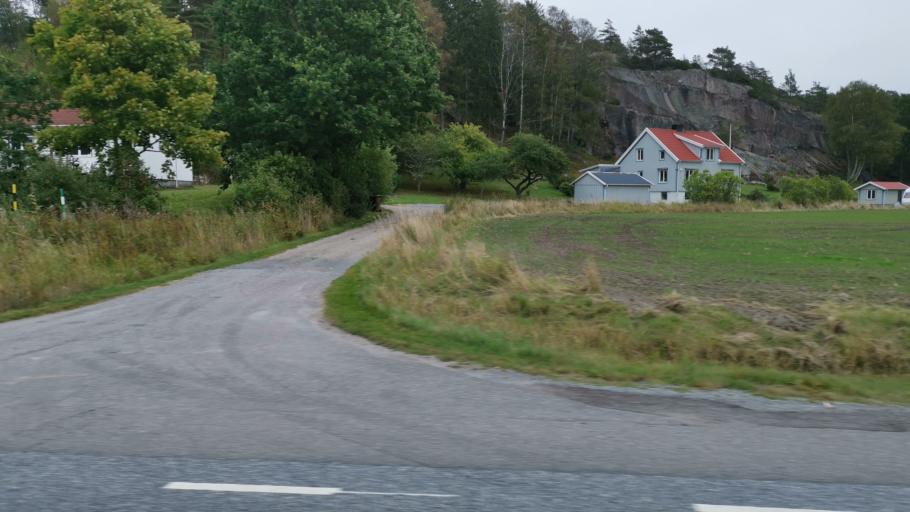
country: SE
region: Vaestra Goetaland
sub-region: Tanums Kommun
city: Tanumshede
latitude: 58.6802
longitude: 11.3384
